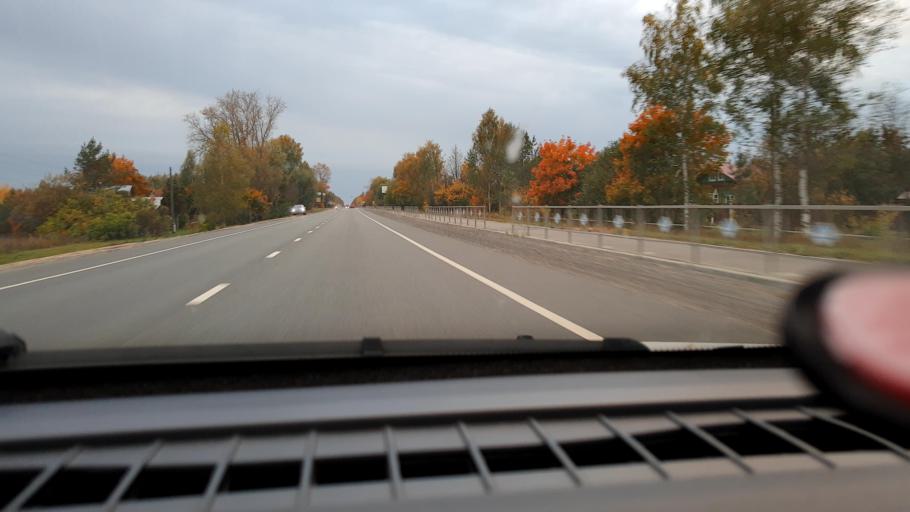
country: RU
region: Vladimir
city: Kameshkovo
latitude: 56.1981
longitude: 40.8488
